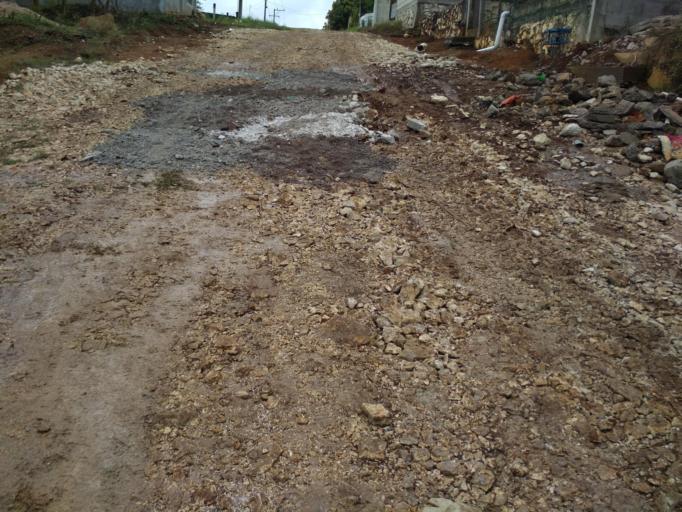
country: MX
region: Veracruz
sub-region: Cordoba
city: San Jose de Tapia
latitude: 18.8516
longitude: -96.9668
